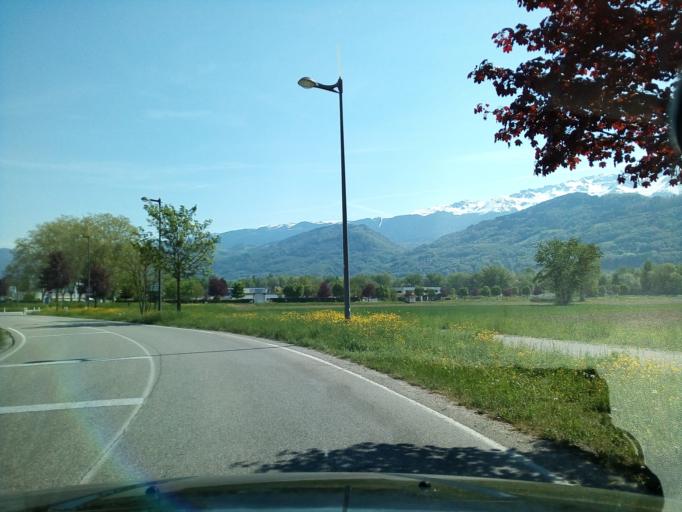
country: FR
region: Rhone-Alpes
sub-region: Departement de l'Isere
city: Crolles
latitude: 45.2670
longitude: 5.8854
